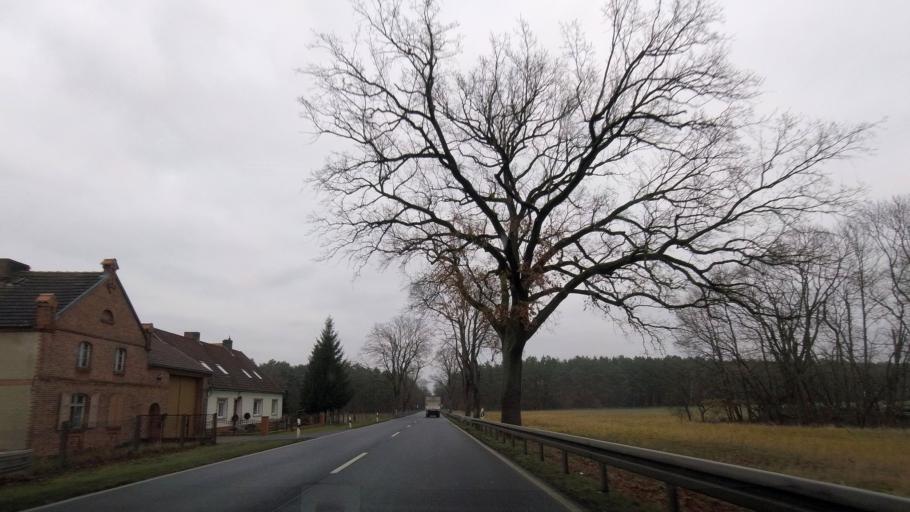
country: DE
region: Brandenburg
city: Beelitz
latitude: 52.2126
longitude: 12.9640
